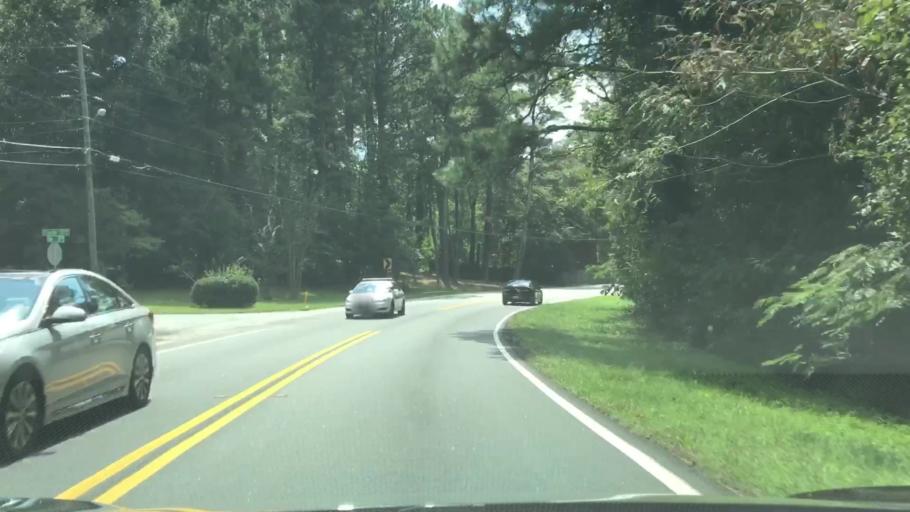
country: US
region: Georgia
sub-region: Gwinnett County
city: Snellville
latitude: 33.8981
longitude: -84.0663
